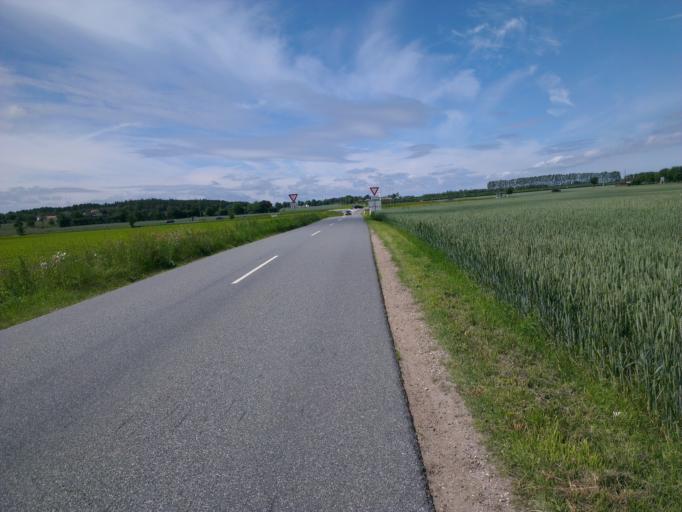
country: DK
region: Capital Region
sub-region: Frederikssund Kommune
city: Skibby
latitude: 55.7894
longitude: 11.9811
